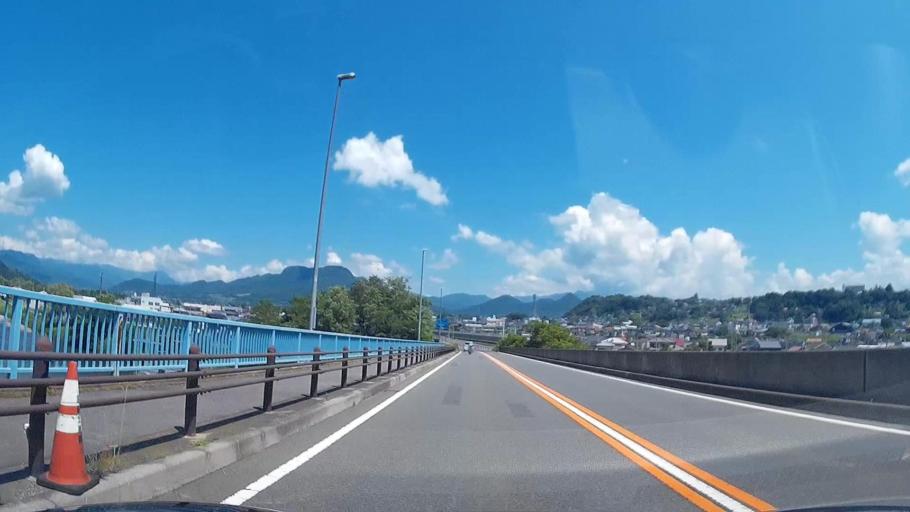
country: JP
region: Gunma
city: Numata
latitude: 36.6377
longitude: 139.0308
